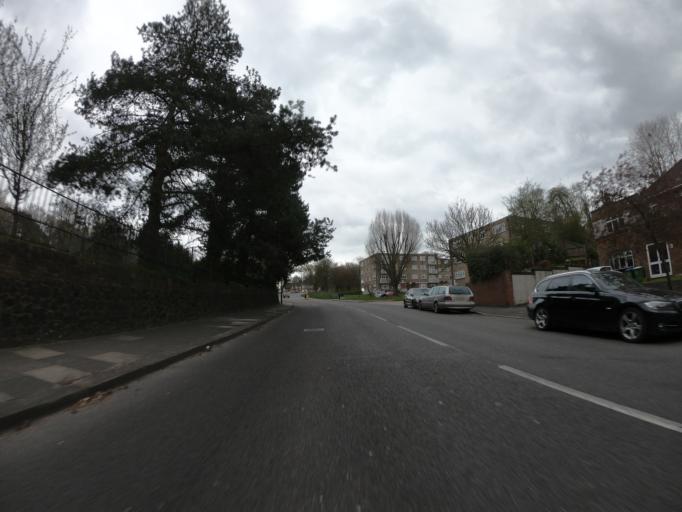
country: GB
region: England
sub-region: Greater London
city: Welling
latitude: 51.4743
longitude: 0.1104
